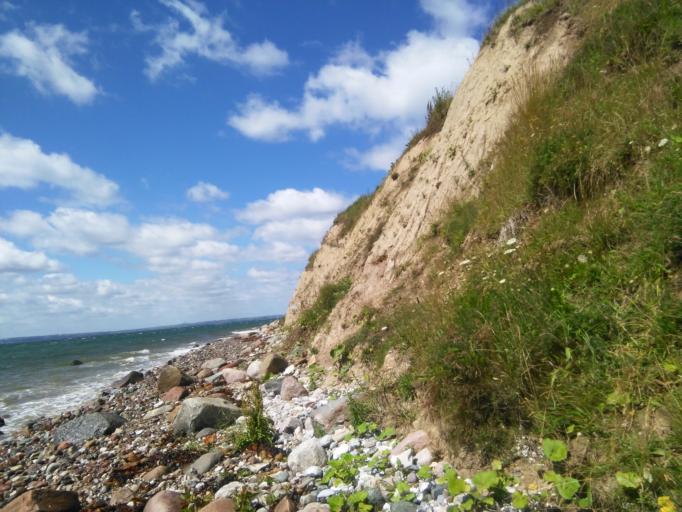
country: DK
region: Central Jutland
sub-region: Arhus Kommune
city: Logten
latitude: 56.1670
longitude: 10.3807
